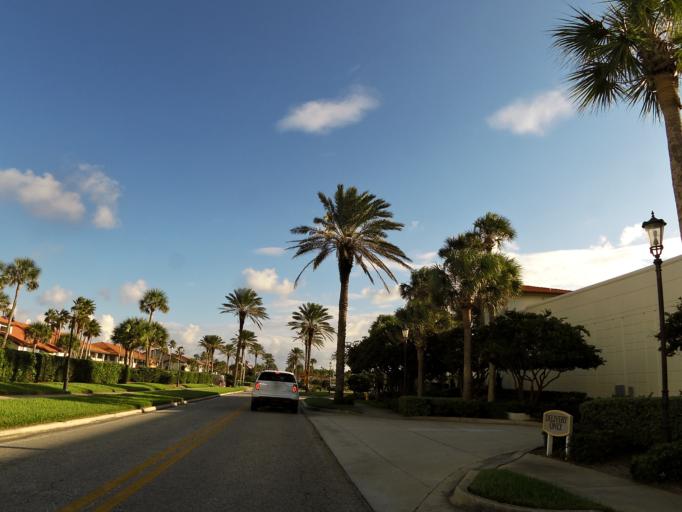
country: US
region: Florida
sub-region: Saint Johns County
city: Ponte Vedra Beach
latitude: 30.2434
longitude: -81.3791
